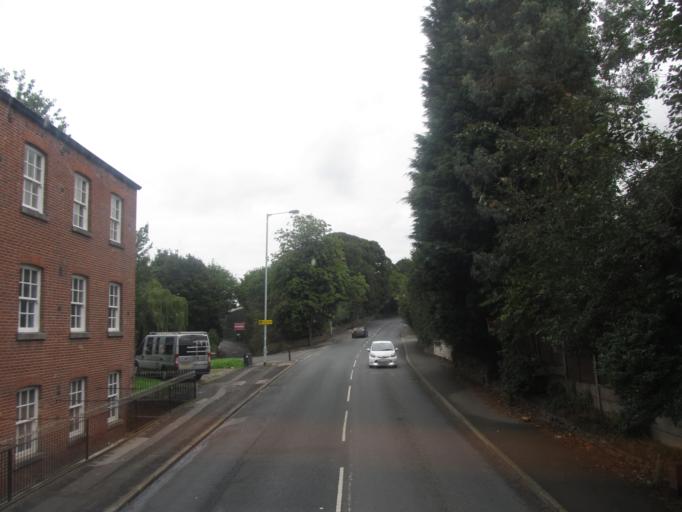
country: GB
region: England
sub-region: Borough of Tameside
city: Haughton Green
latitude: 53.4286
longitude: -2.0948
